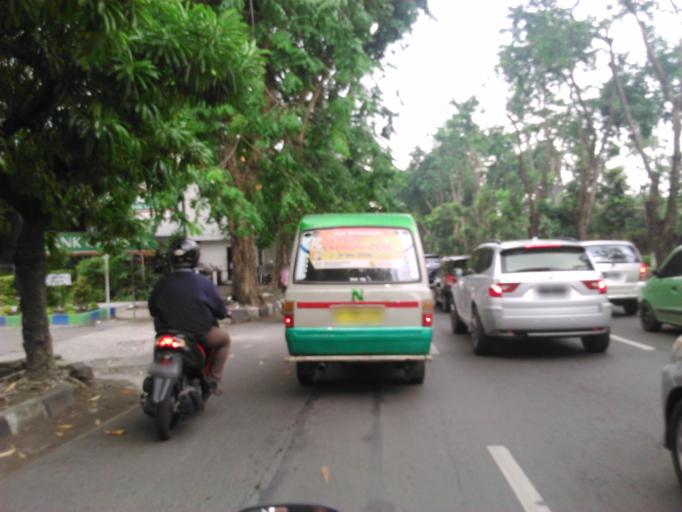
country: ID
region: East Java
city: Gubengairlangga
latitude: -7.2790
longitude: 112.7593
